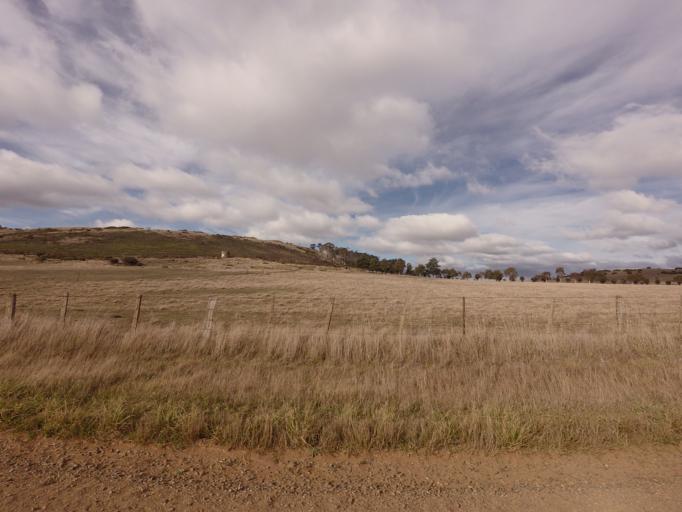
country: AU
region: Tasmania
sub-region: Brighton
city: Bridgewater
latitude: -42.4185
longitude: 147.3933
